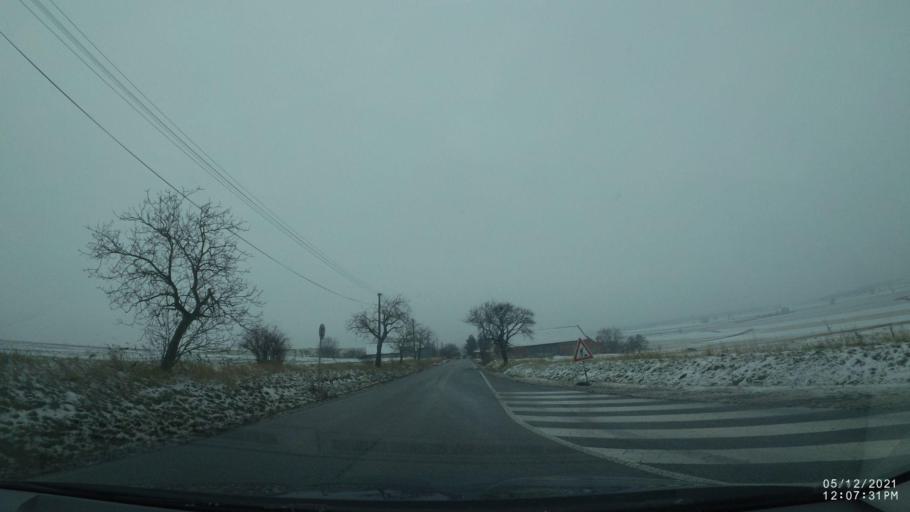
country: CZ
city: Ceske Mezirici
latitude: 50.2966
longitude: 16.0161
